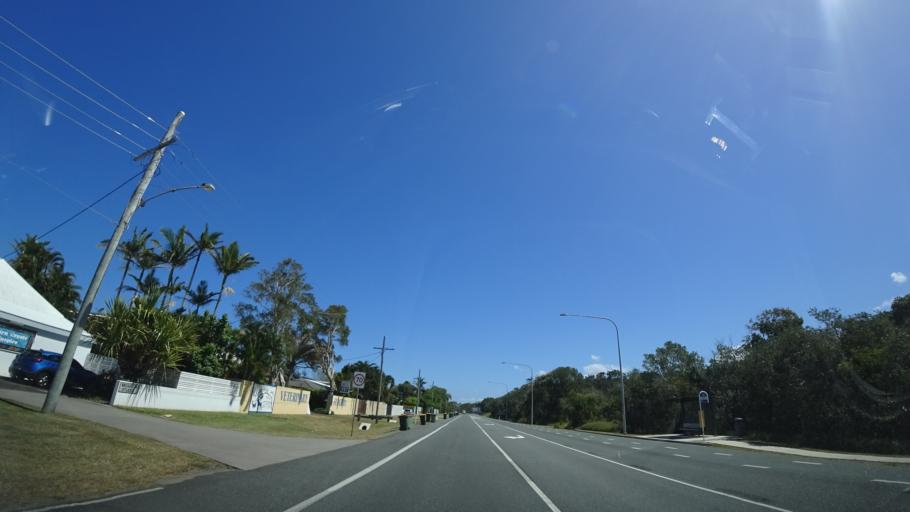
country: AU
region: Queensland
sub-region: Sunshine Coast
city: Coolum Beach
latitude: -26.5844
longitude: 153.0931
